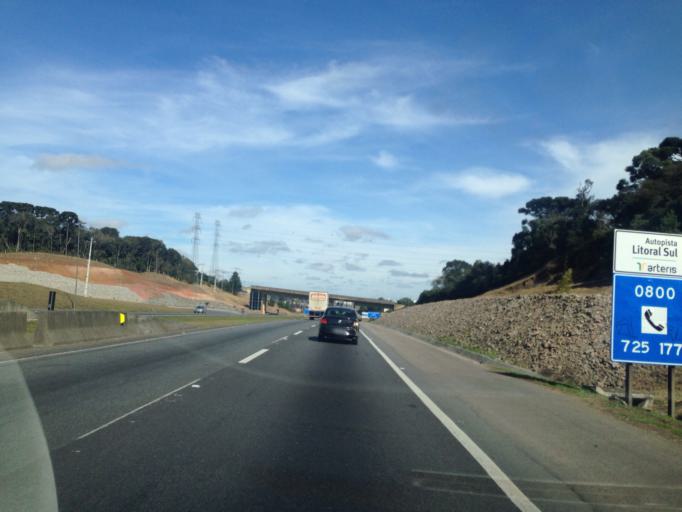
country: BR
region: Parana
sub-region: Sao Jose Dos Pinhais
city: Sao Jose dos Pinhais
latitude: -25.5181
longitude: -49.1330
